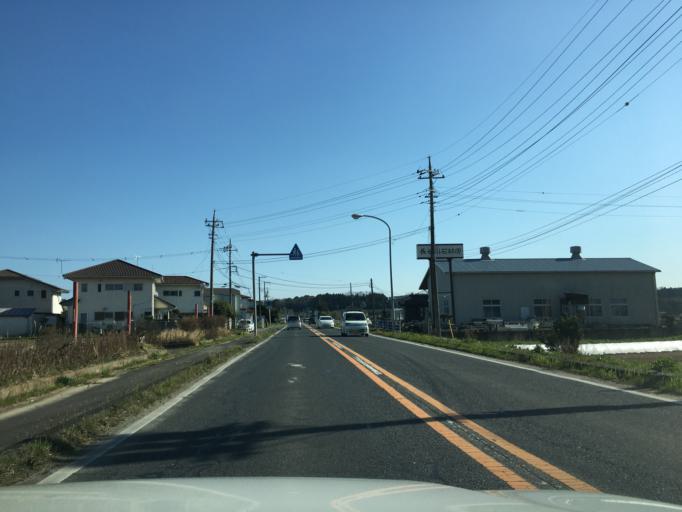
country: JP
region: Ibaraki
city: Omiya
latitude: 36.4494
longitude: 140.4092
